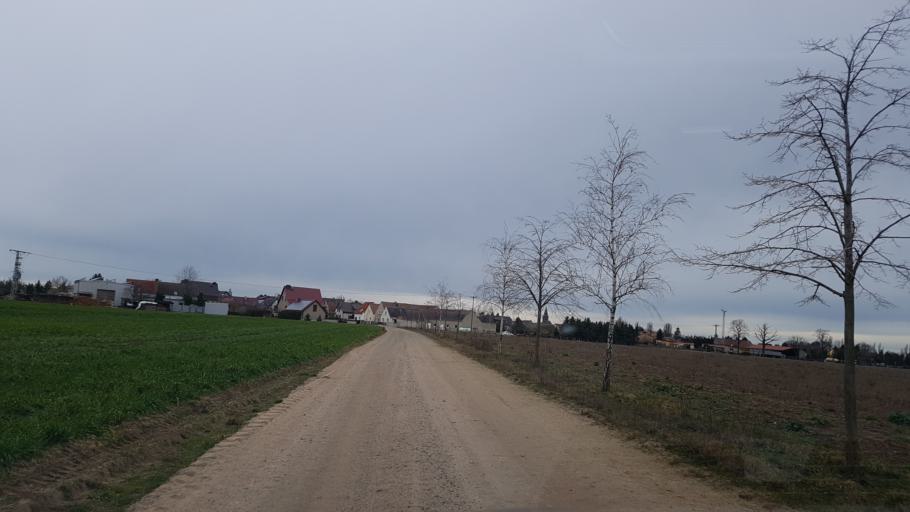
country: DE
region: Brandenburg
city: Bad Liebenwerda
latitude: 51.4909
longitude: 13.3425
